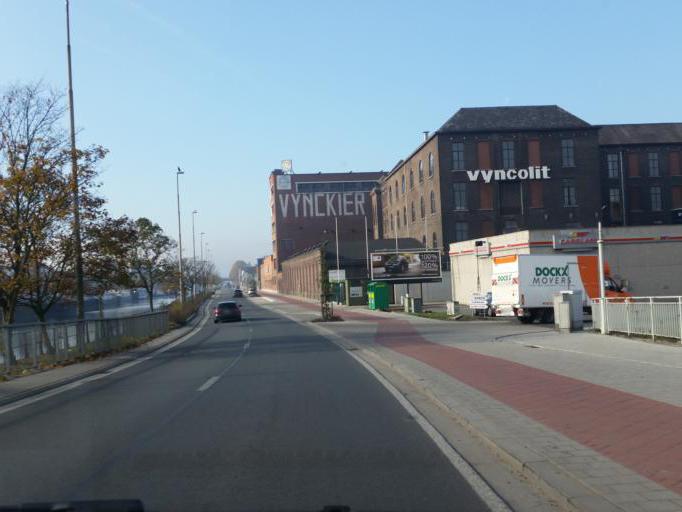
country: BE
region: Flanders
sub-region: Provincie Oost-Vlaanderen
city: Gent
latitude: 51.0684
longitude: 3.7258
